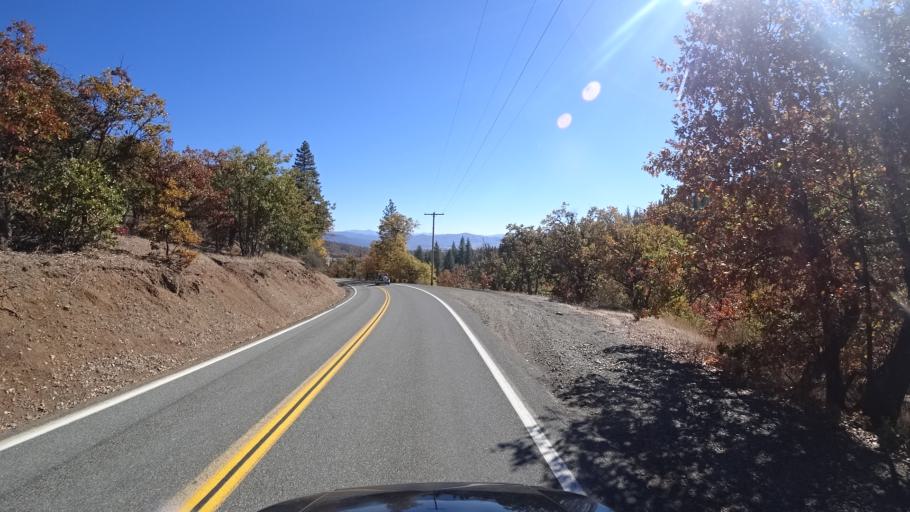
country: US
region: California
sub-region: Siskiyou County
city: Yreka
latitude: 41.5664
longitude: -122.9367
